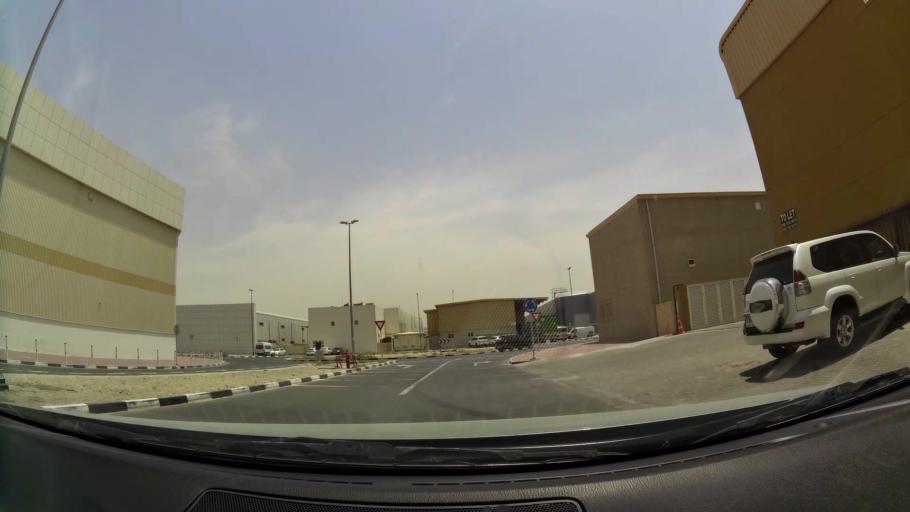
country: AE
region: Ash Shariqah
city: Sharjah
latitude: 25.1873
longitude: 55.3813
